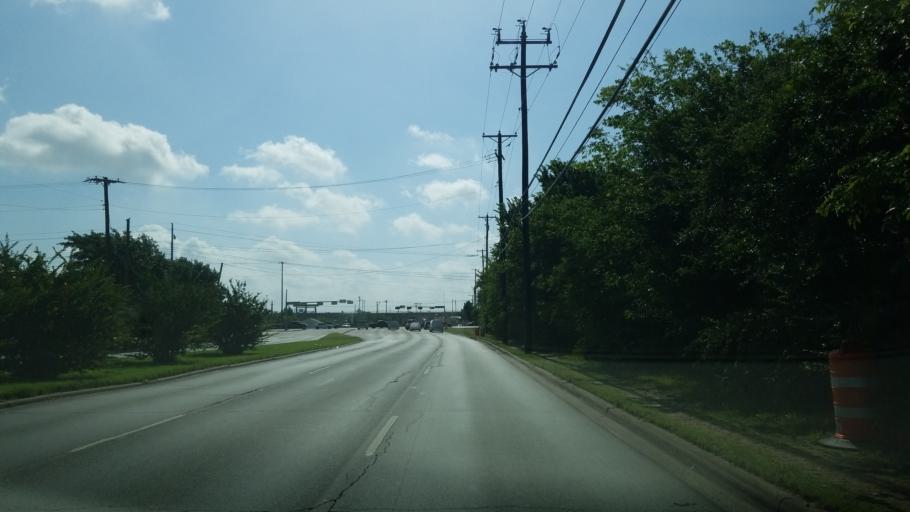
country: US
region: Texas
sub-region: Dallas County
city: Farmers Branch
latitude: 32.8809
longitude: -96.8871
